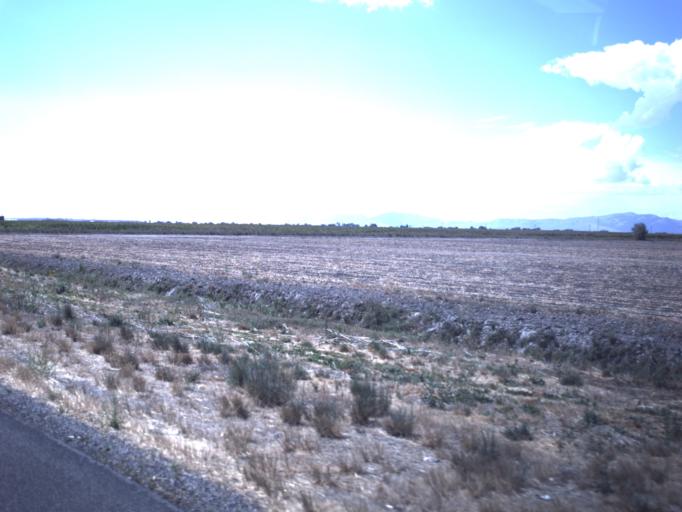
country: US
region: Utah
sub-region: Box Elder County
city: Honeyville
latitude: 41.5888
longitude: -112.1298
